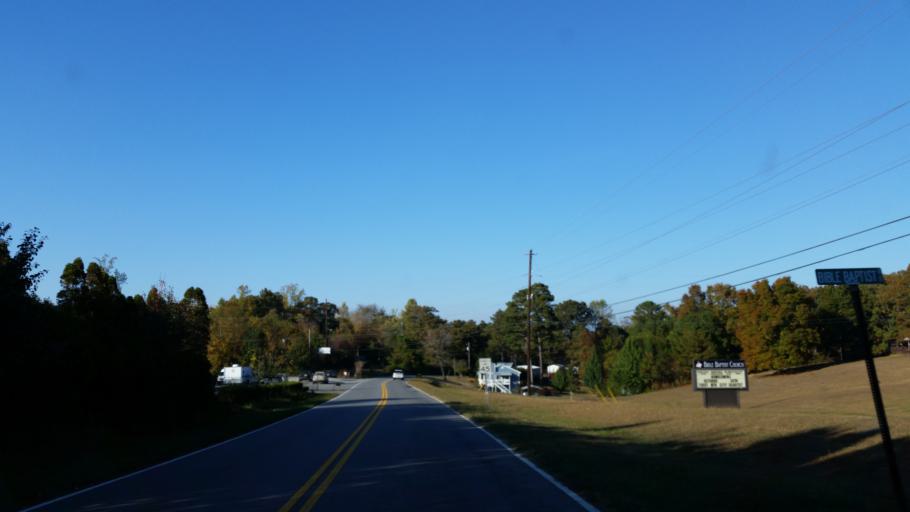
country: US
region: Georgia
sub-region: Gilmer County
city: Ellijay
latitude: 34.6419
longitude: -84.4714
